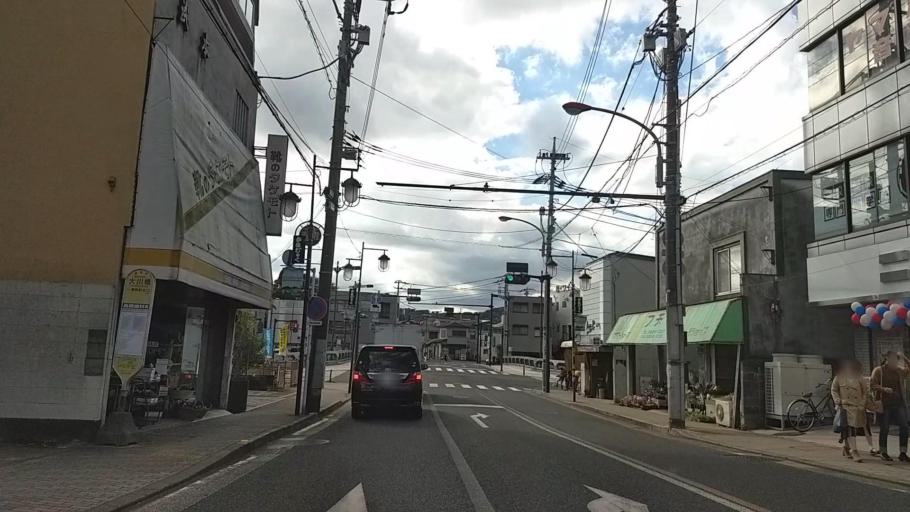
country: JP
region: Kanagawa
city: Hadano
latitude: 35.3728
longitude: 139.2251
